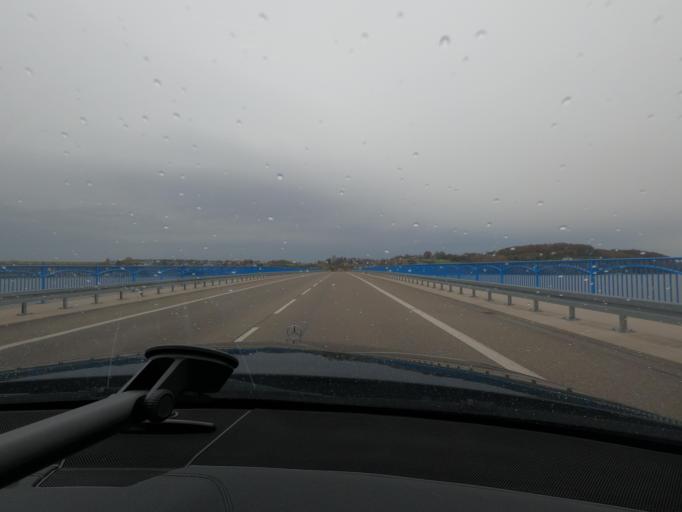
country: DE
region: North Rhine-Westphalia
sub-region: Regierungsbezirk Arnsberg
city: Mohnesee
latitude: 51.4835
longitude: 8.0867
